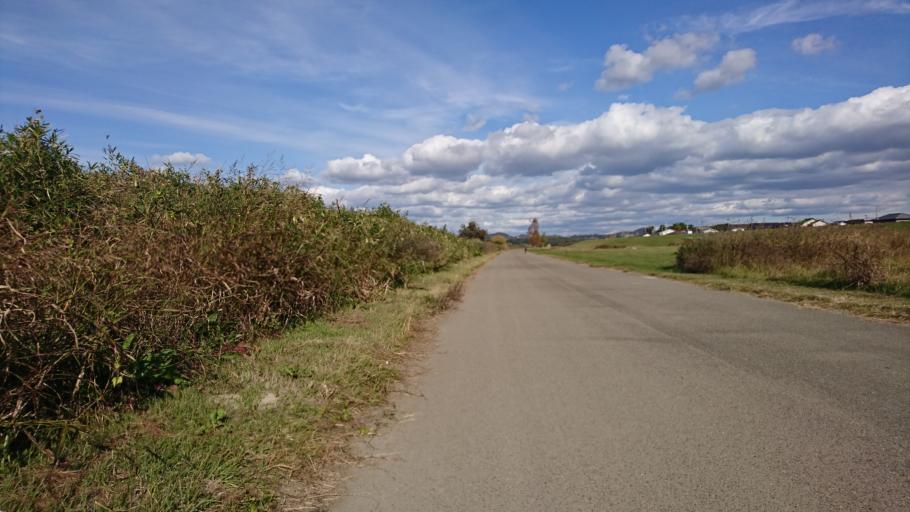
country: JP
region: Hyogo
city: Kakogawacho-honmachi
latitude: 34.7904
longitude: 134.8685
